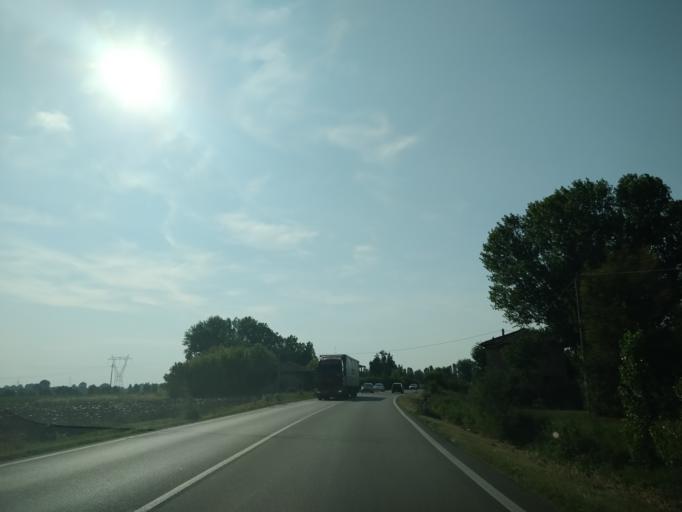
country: IT
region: Emilia-Romagna
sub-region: Provincia di Bologna
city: Castel Maggiore
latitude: 44.6032
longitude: 11.3386
